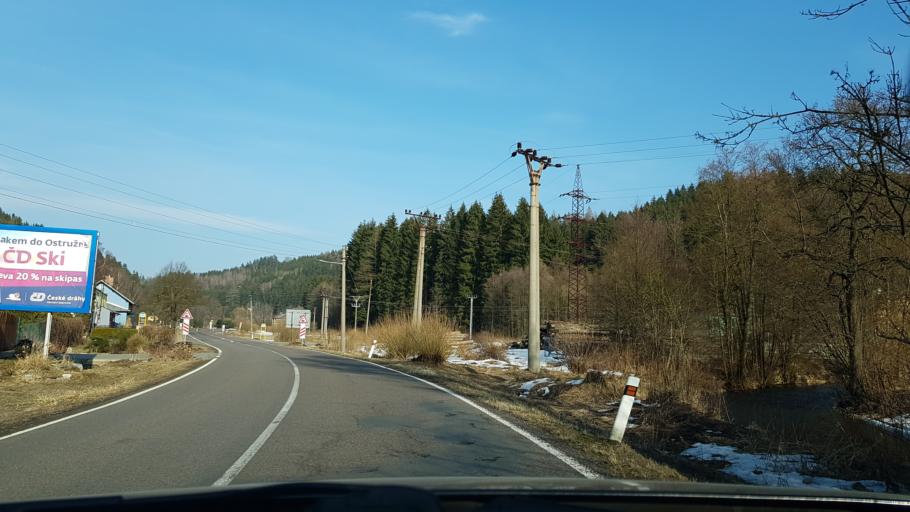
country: CZ
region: Olomoucky
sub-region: Okres Sumperk
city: Hanusovice
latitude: 50.0788
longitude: 16.9619
